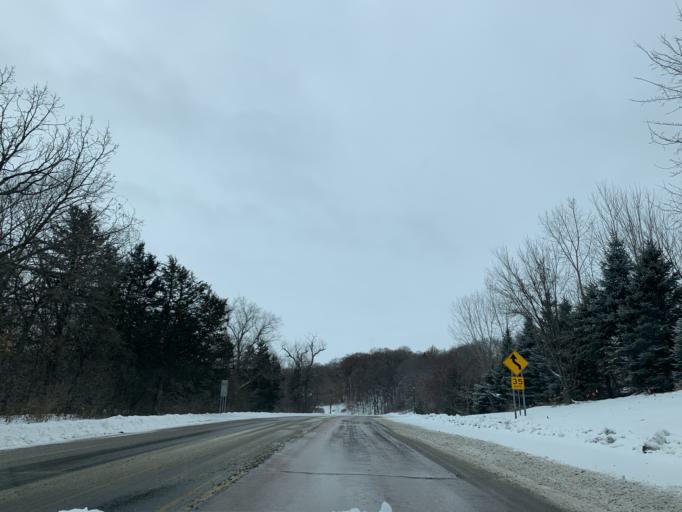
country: US
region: Minnesota
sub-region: Carver County
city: Chaska
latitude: 44.7866
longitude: -93.6097
